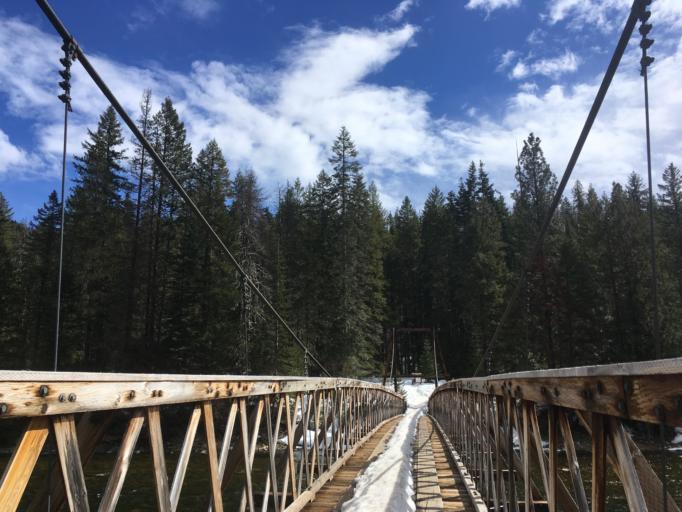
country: US
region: Montana
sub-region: Mineral County
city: Superior
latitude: 46.4745
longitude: -114.8854
